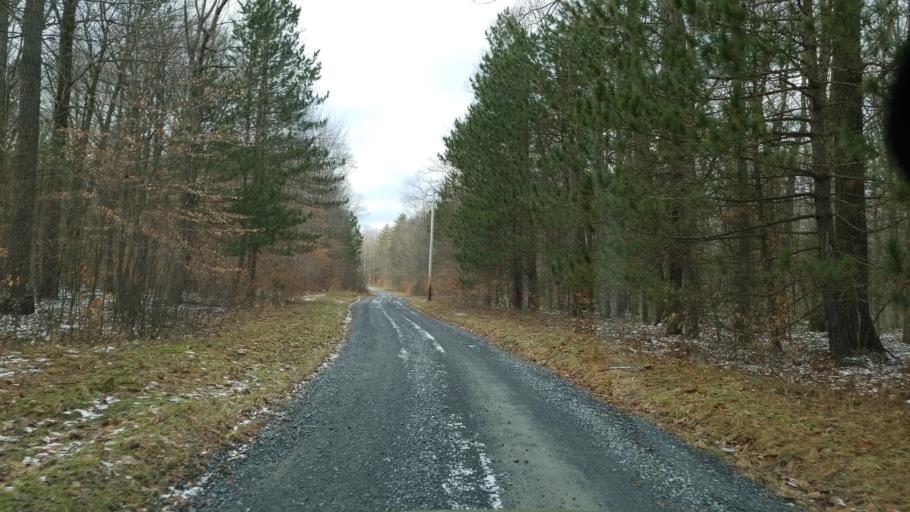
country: US
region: Pennsylvania
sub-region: Clearfield County
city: Clearfield
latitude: 41.1355
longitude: -78.5232
